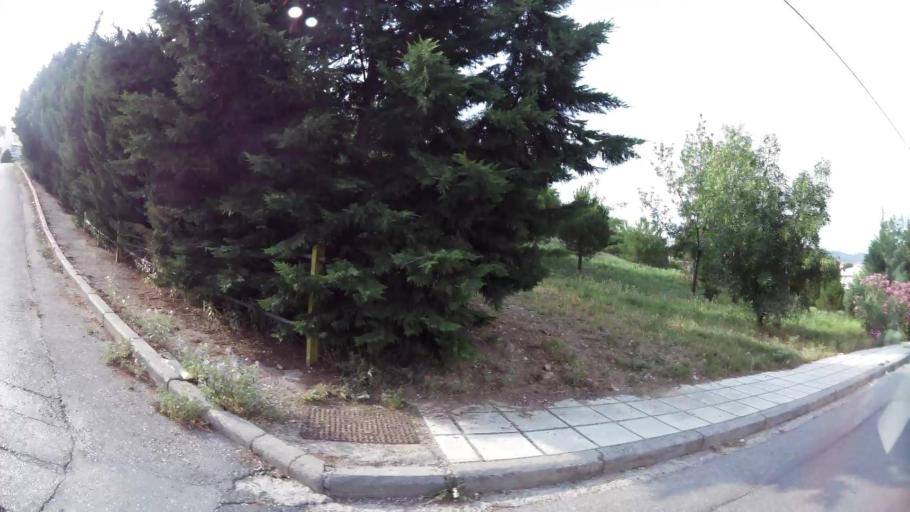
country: GR
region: Central Macedonia
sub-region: Nomos Thessalonikis
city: Oraiokastro
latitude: 40.7208
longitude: 22.9175
